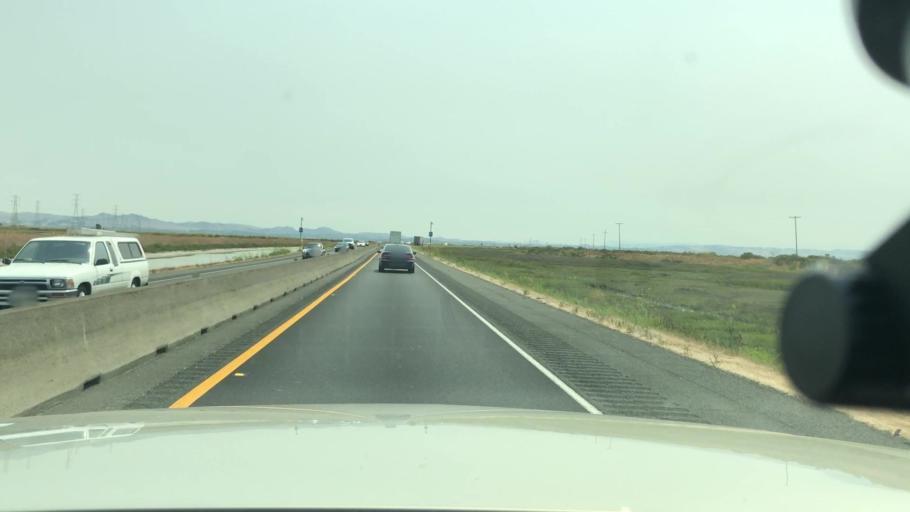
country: US
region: California
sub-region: Marin County
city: Black Point-Green Point
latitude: 38.1521
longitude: -122.3892
